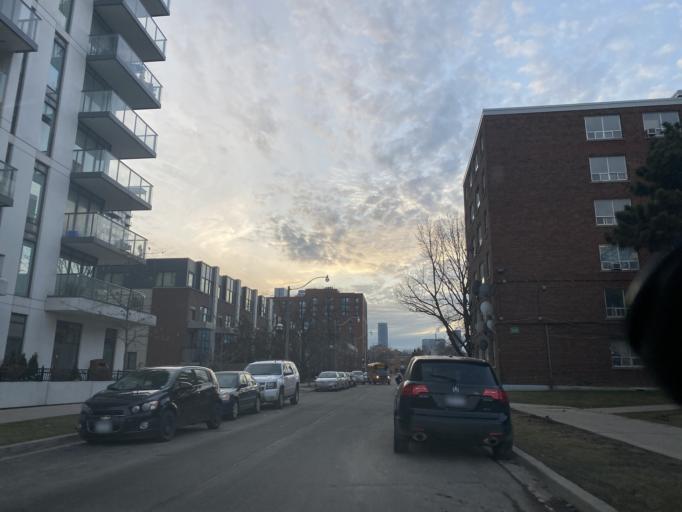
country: CA
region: Ontario
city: Toronto
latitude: 43.6614
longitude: -79.3637
